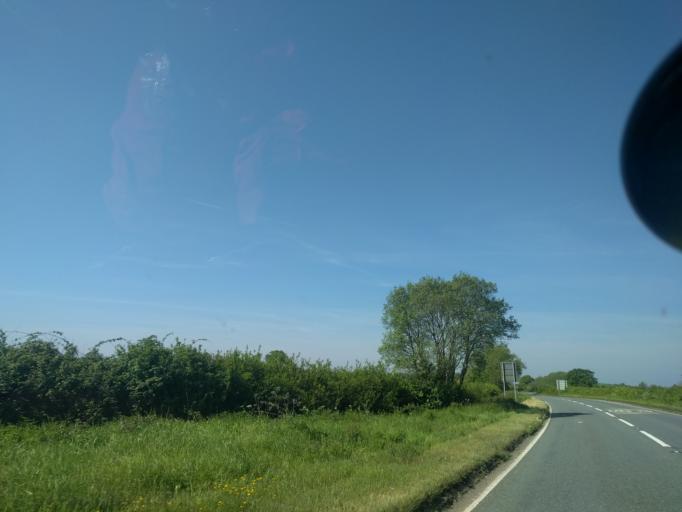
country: GB
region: England
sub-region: Somerset
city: Ilchester
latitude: 51.0260
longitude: -2.6726
